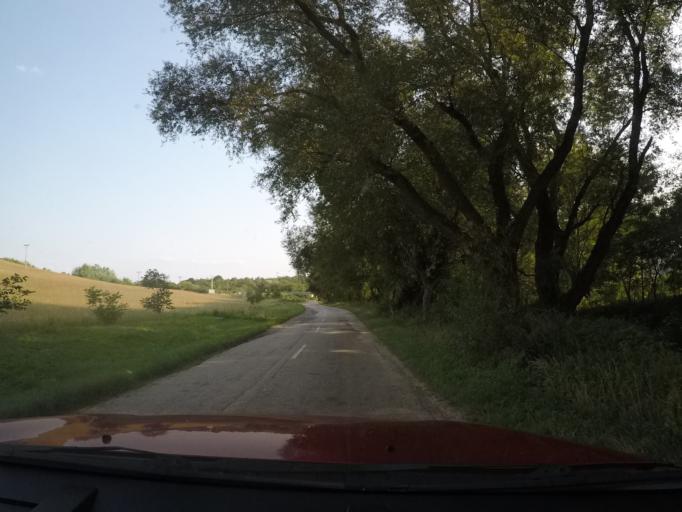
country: SK
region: Kosicky
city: Medzev
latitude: 48.6078
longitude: 20.8368
